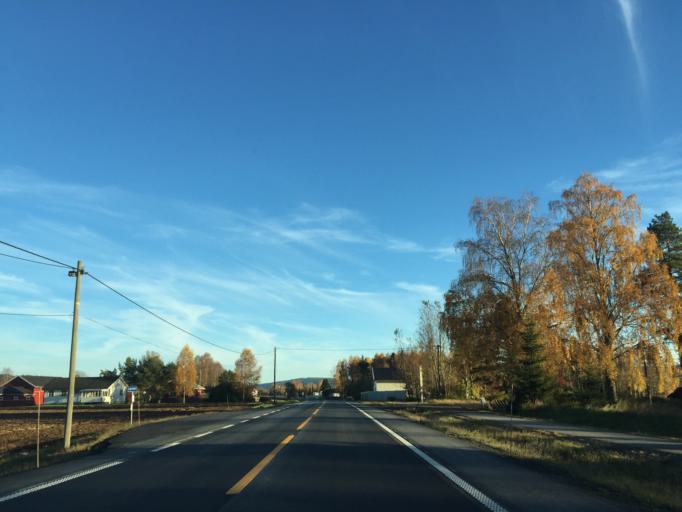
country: NO
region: Hedmark
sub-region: Kongsvinger
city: Spetalen
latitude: 60.2356
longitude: 11.8004
